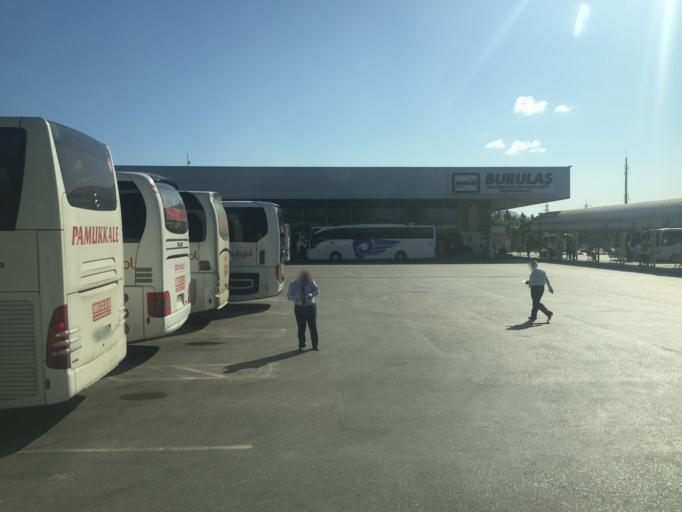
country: TR
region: Bursa
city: Demirtas
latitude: 40.2645
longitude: 29.0523
